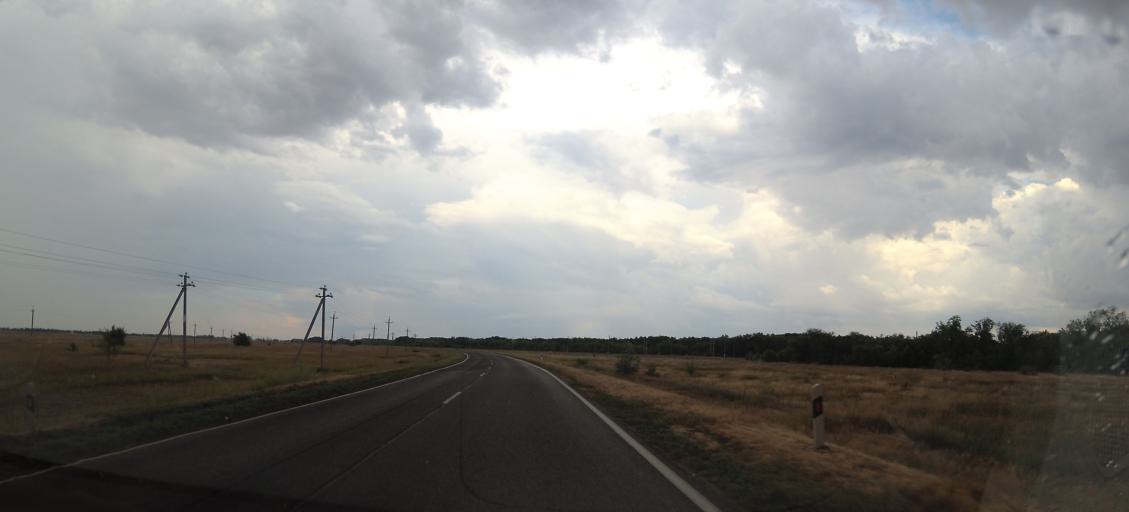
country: RU
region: Rostov
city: Dubovskoye
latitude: 47.2953
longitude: 42.6144
